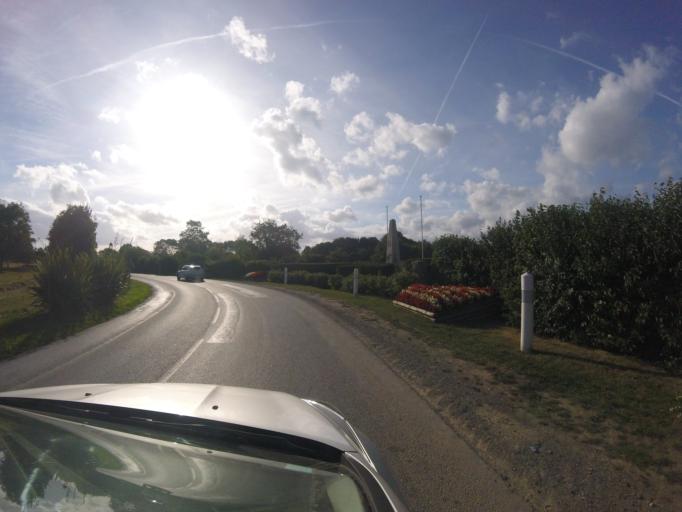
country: FR
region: Lower Normandy
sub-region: Departement du Calvados
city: Port-en-Bessin-Huppain
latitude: 49.3485
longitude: -0.8487
